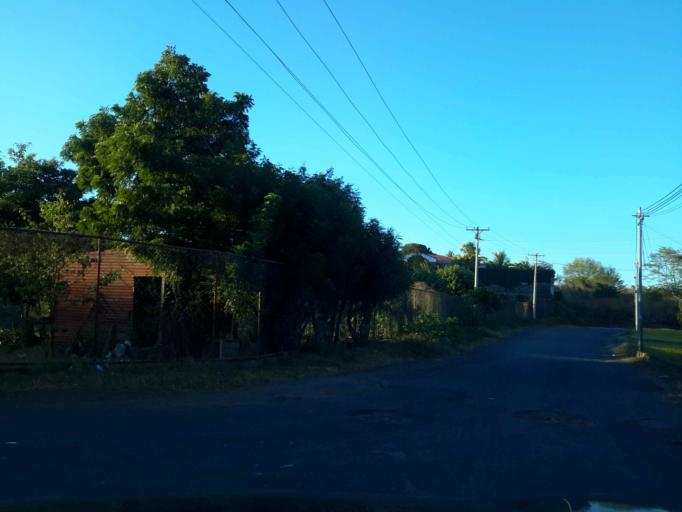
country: NI
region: Managua
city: Managua
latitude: 12.0942
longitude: -86.2246
